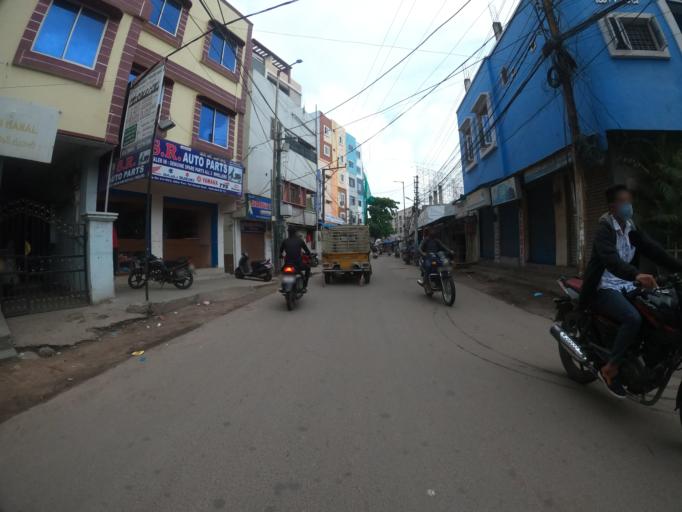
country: IN
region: Telangana
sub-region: Hyderabad
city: Hyderabad
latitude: 17.3974
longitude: 78.4173
